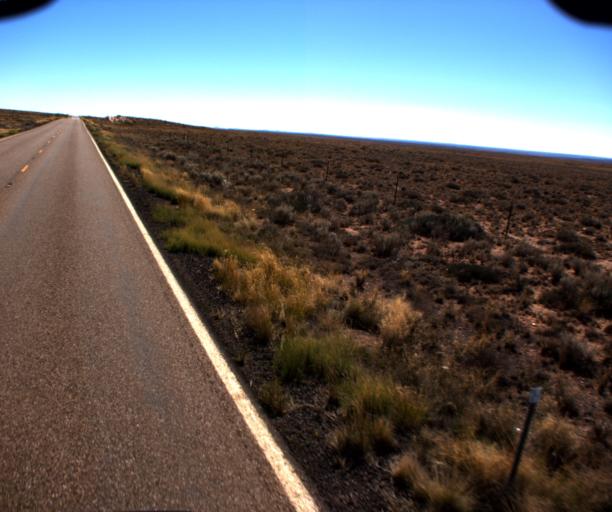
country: US
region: Arizona
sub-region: Navajo County
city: Holbrook
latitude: 35.0171
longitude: -110.0901
